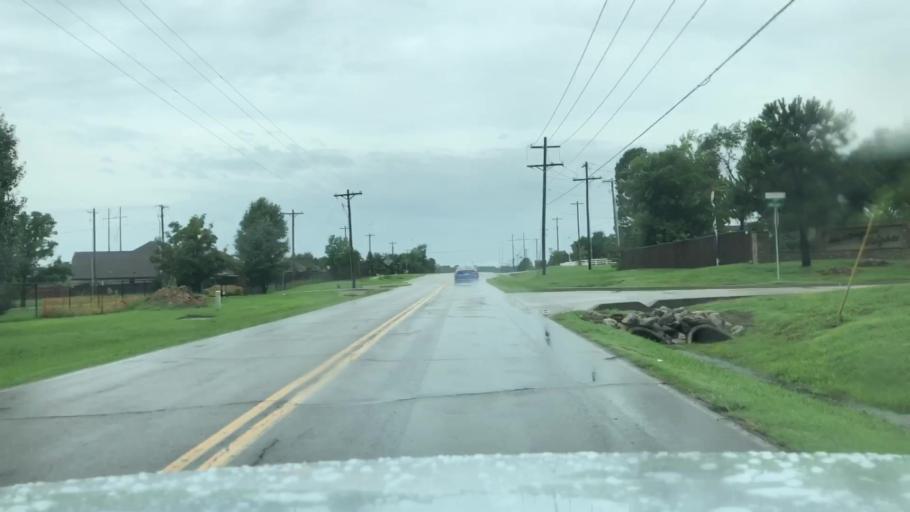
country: US
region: Oklahoma
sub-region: Tulsa County
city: Jenks
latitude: 36.0028
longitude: -96.0020
